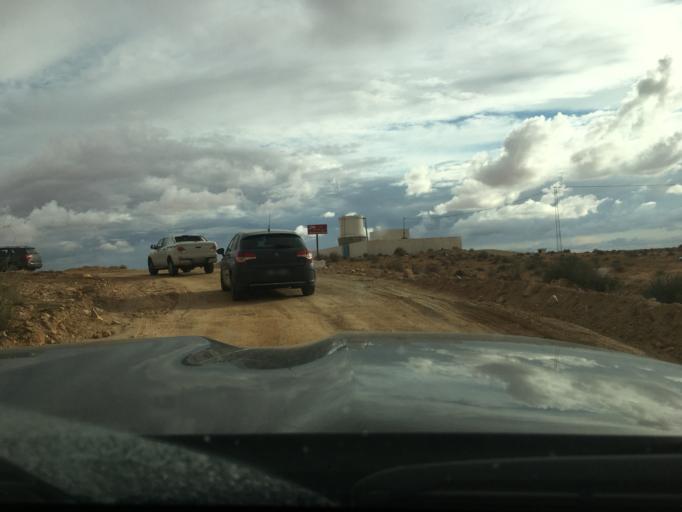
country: TN
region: Madanin
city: Medenine
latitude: 33.2671
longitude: 10.5694
